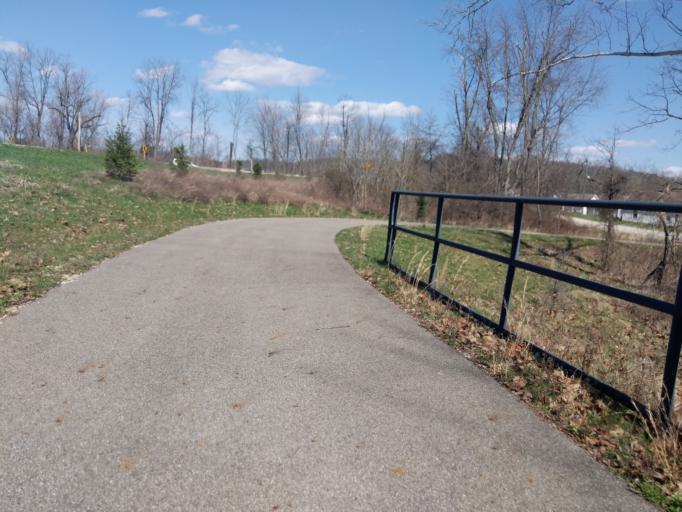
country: US
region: Ohio
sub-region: Athens County
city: The Plains
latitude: 39.3644
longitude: -82.1196
